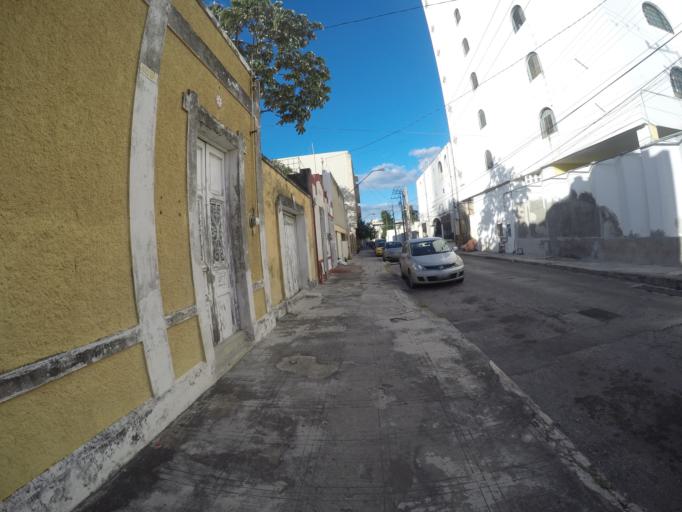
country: MX
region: Yucatan
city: Merida
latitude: 20.9793
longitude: -89.6195
